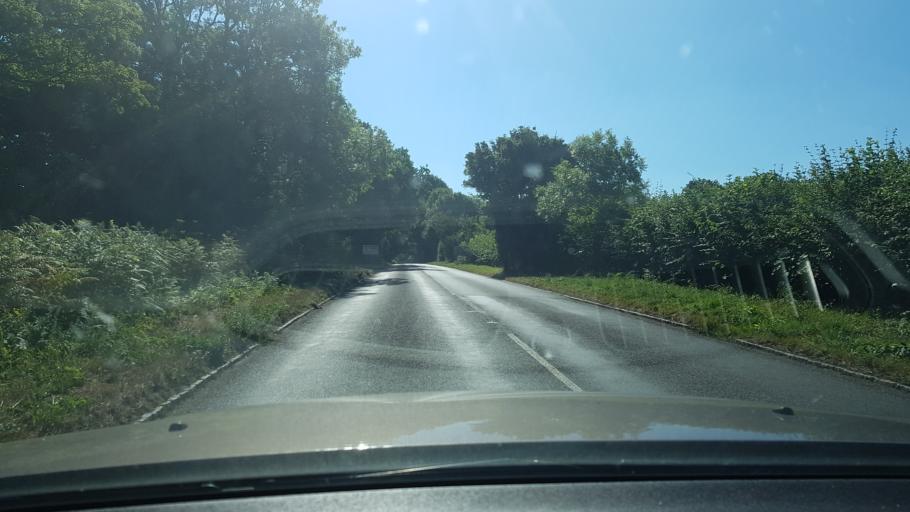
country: GB
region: England
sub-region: West Berkshire
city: Lambourn
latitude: 51.4747
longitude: -1.5245
